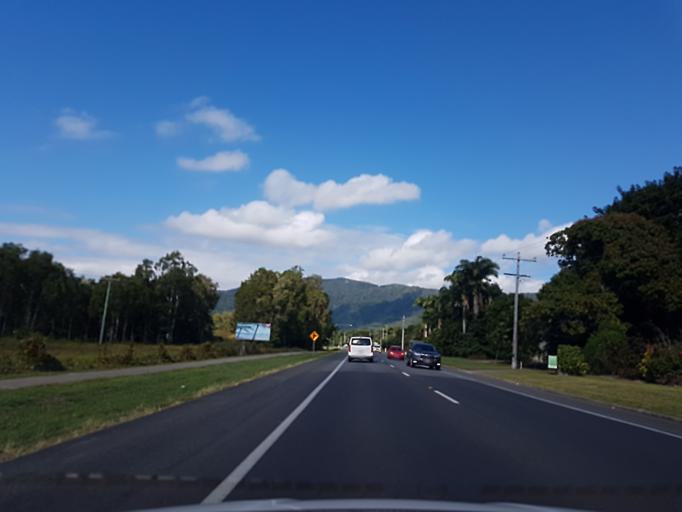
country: AU
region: Queensland
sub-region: Cairns
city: Trinity Beach
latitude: -16.7797
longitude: 145.6743
